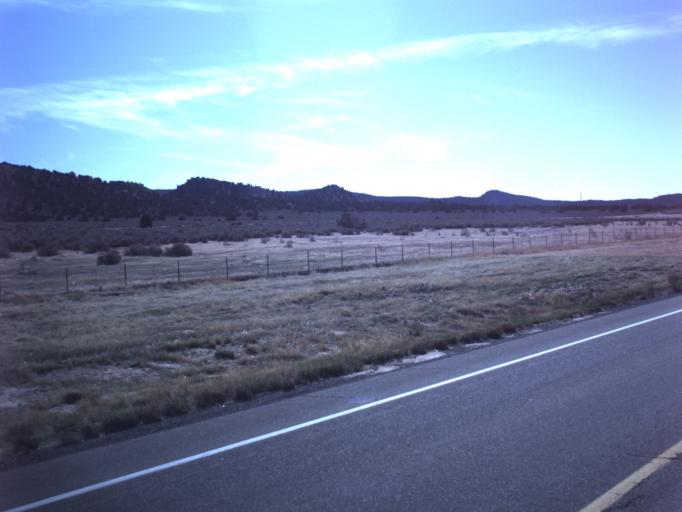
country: US
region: Utah
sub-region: Sanpete County
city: Gunnison
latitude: 39.3988
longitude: -111.9279
